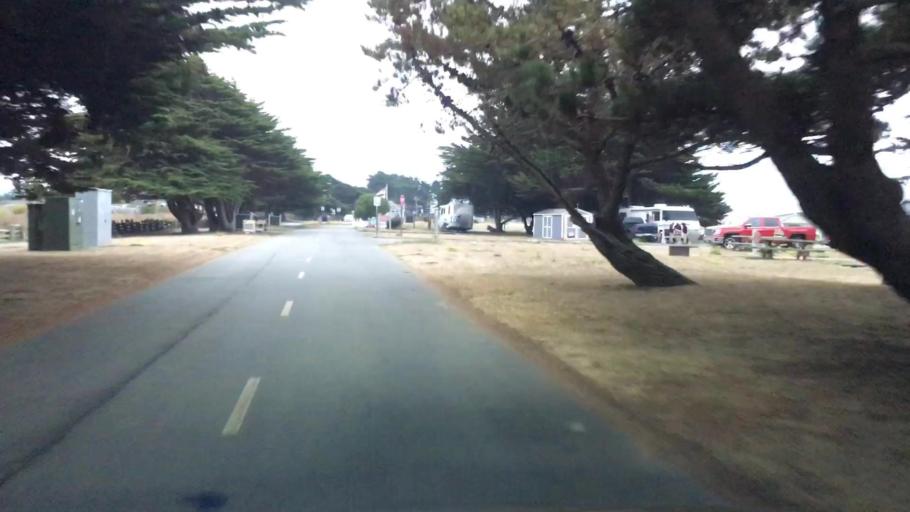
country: US
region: California
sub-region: San Mateo County
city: Half Moon Bay
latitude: 37.4684
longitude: -122.4451
